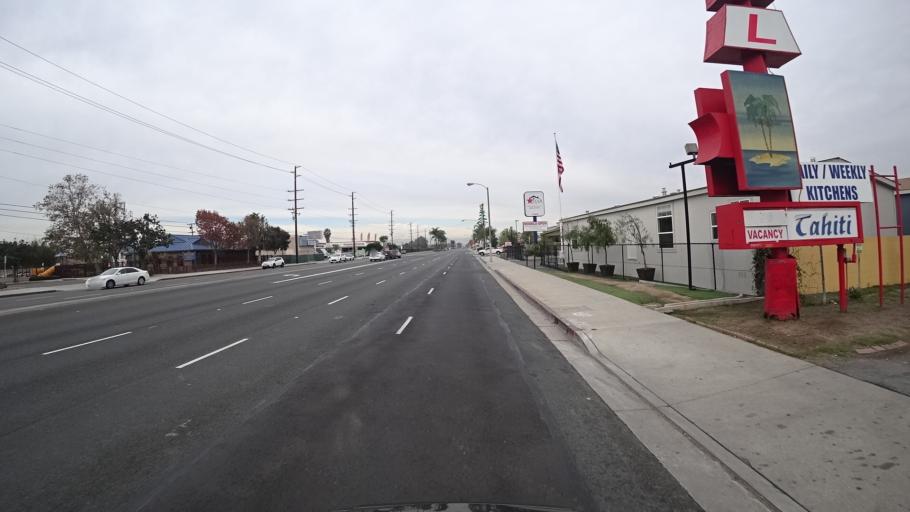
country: US
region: California
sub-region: Orange County
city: Stanton
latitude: 33.7903
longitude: -117.9928
